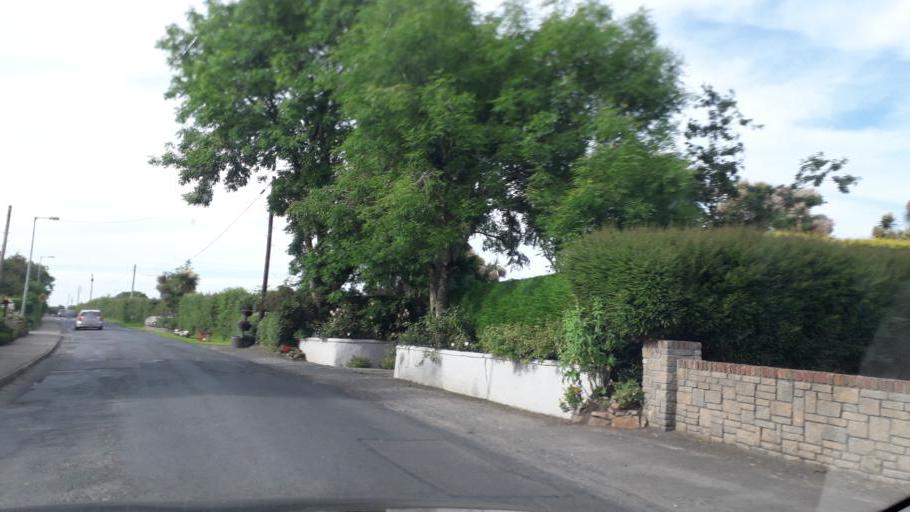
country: IE
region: Leinster
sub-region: Loch Garman
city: Courtown
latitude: 52.5748
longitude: -6.2297
